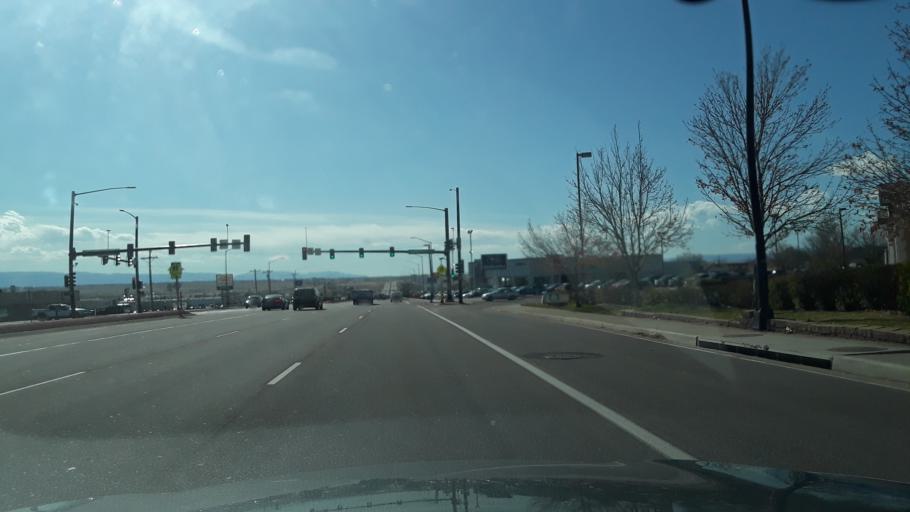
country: US
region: Colorado
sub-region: Pueblo County
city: Pueblo
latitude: 38.3102
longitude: -104.6343
